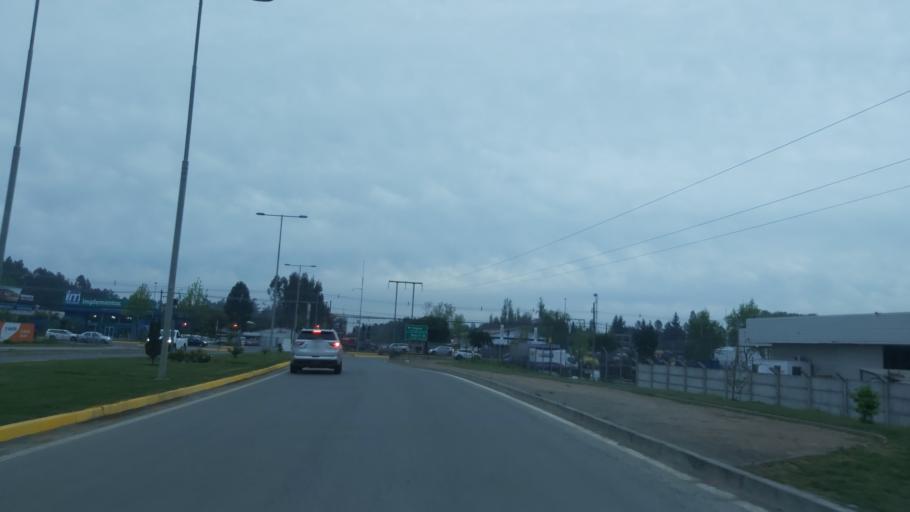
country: CL
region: Maule
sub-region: Provincia de Linares
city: Linares
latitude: -35.8397
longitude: -71.6242
